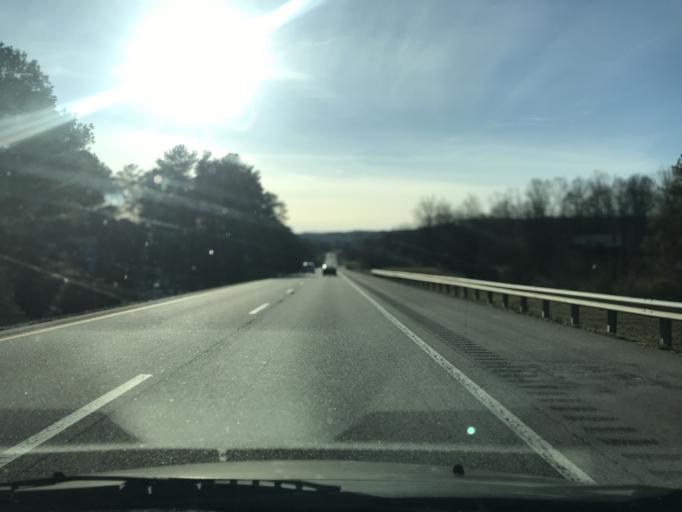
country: US
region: Tennessee
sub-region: Bradley County
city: Cleveland
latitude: 35.1450
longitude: -84.9754
